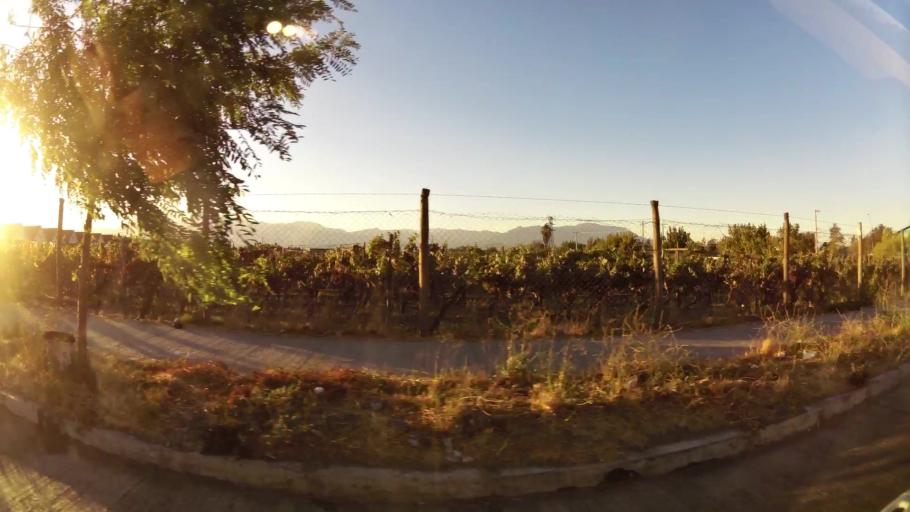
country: CL
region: O'Higgins
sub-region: Provincia de Cachapoal
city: Rancagua
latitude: -34.1885
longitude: -70.7352
